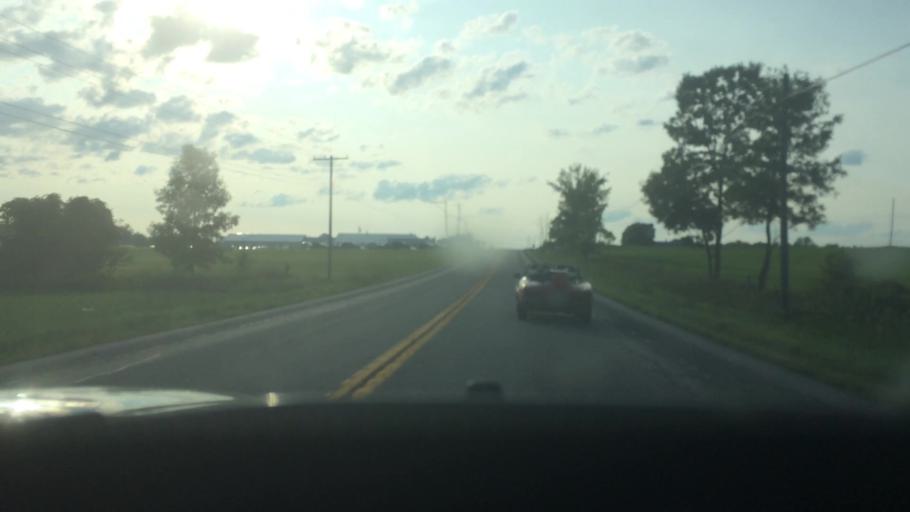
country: US
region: New York
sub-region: St. Lawrence County
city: Ogdensburg
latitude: 44.6669
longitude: -75.3692
